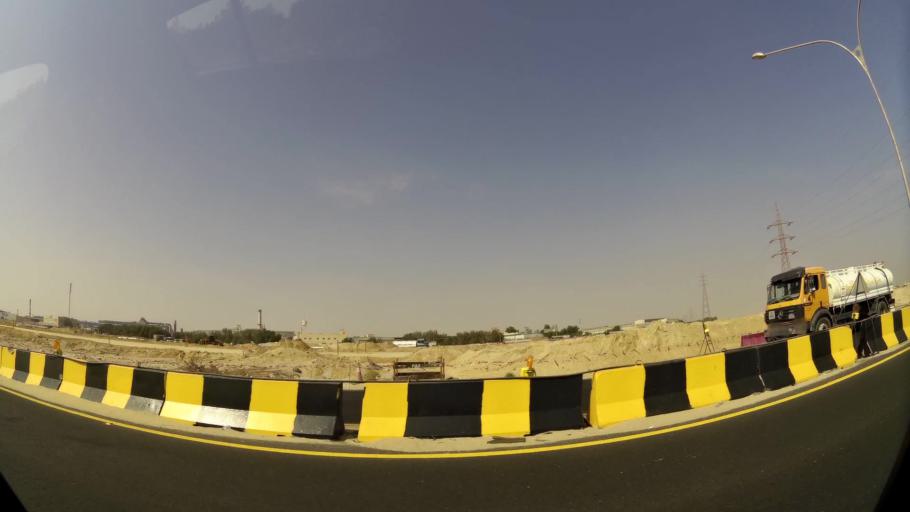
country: KW
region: Al Ahmadi
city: Al Fahahil
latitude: 28.9925
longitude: 48.1406
